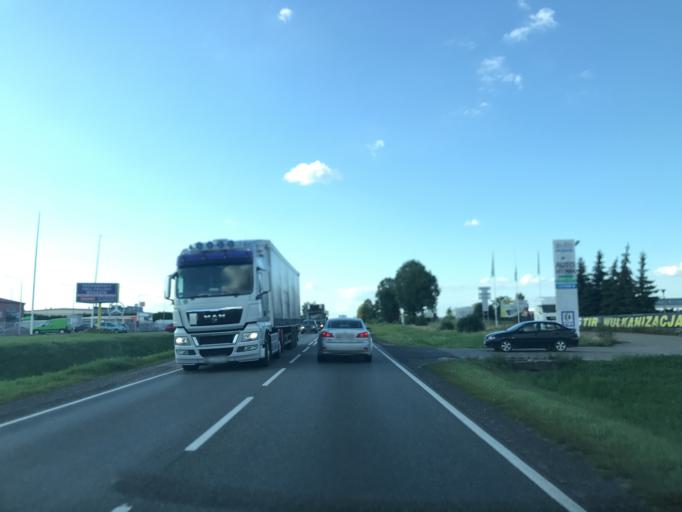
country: PL
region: Kujawsko-Pomorskie
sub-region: Powiat bydgoski
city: Biale Blota
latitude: 53.1317
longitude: 17.8802
